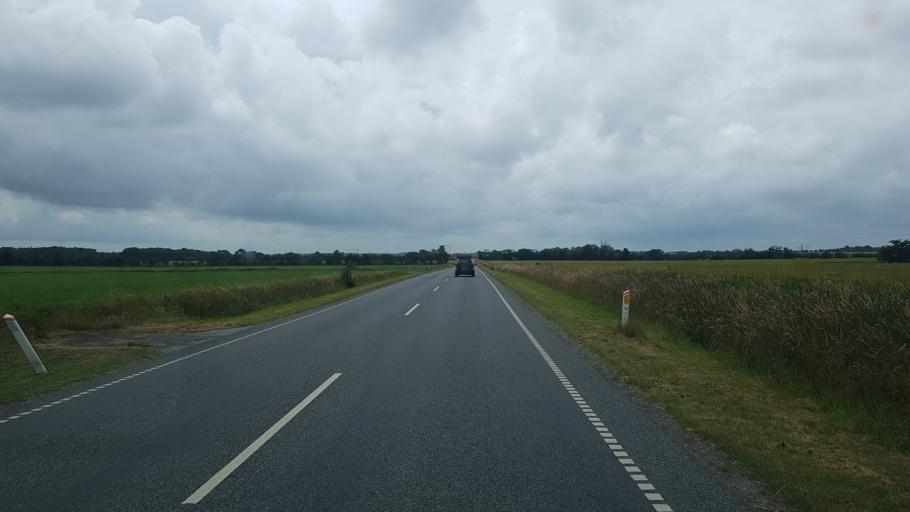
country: DK
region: South Denmark
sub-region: Vejen Kommune
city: Vejen
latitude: 55.4103
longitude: 9.1294
